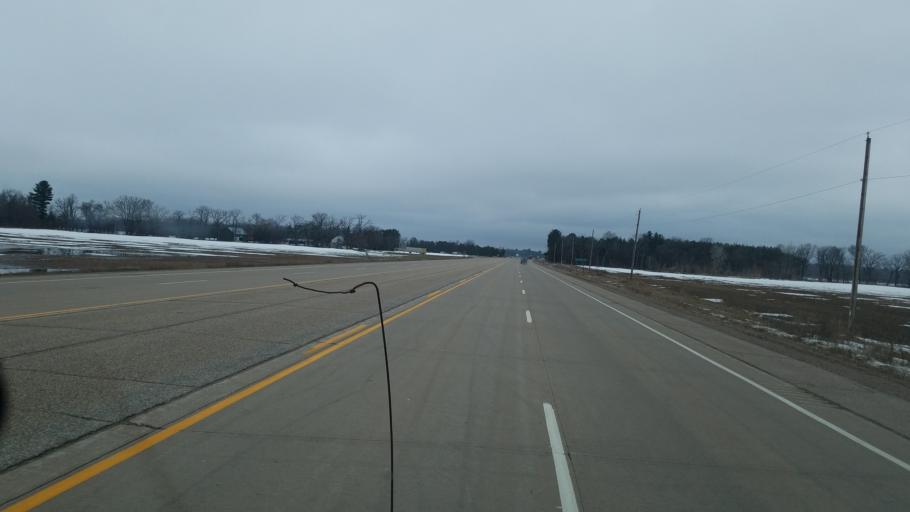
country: US
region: Wisconsin
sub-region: Portage County
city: Whiting
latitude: 44.5223
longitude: -89.4622
